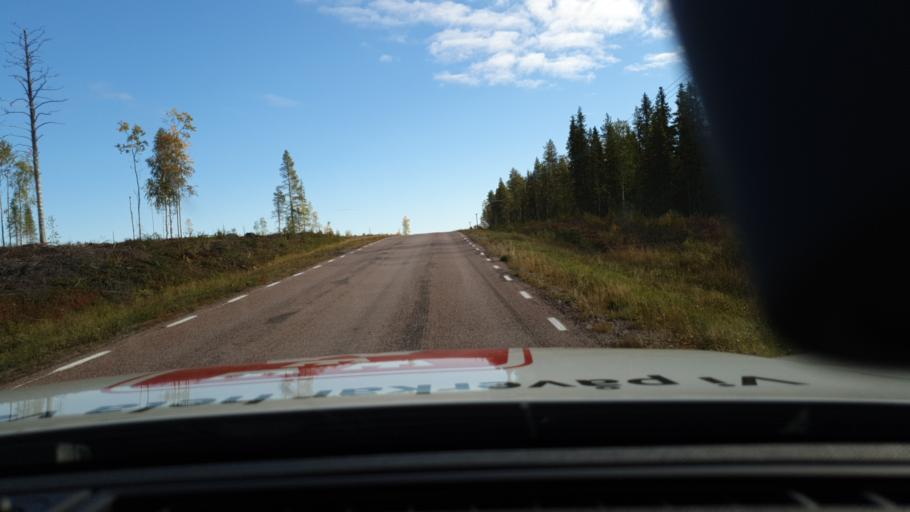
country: SE
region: Norrbotten
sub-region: Pajala Kommun
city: Pajala
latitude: 67.1890
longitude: 23.2988
